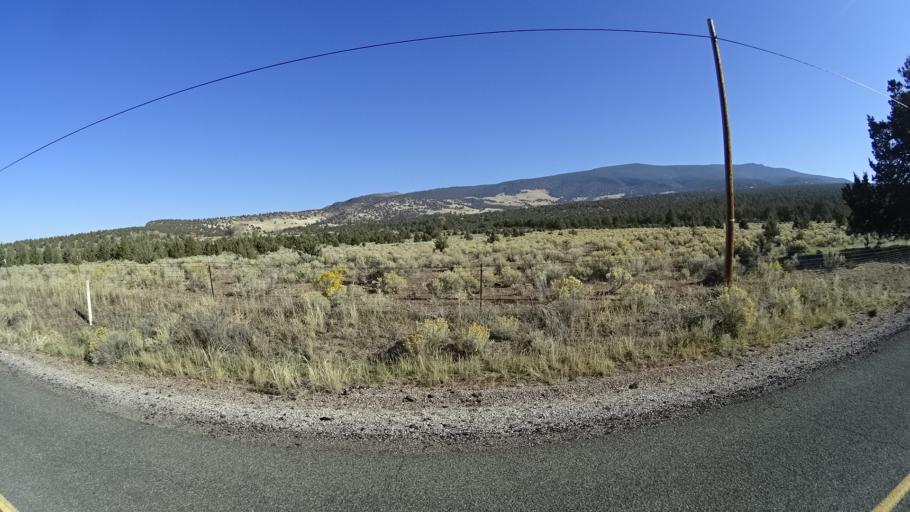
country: US
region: California
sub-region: Siskiyou County
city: Montague
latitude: 41.6354
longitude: -122.3388
